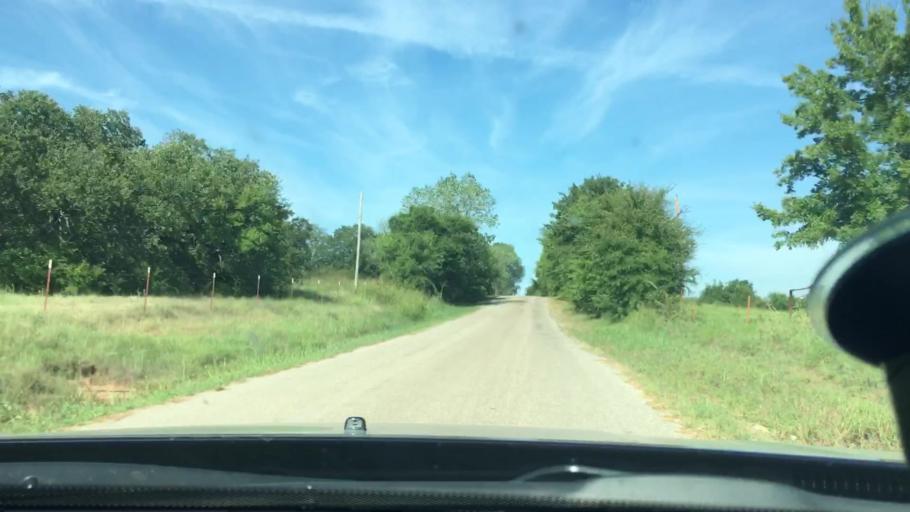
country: US
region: Oklahoma
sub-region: Carter County
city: Lone Grove
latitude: 34.2673
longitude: -97.2729
